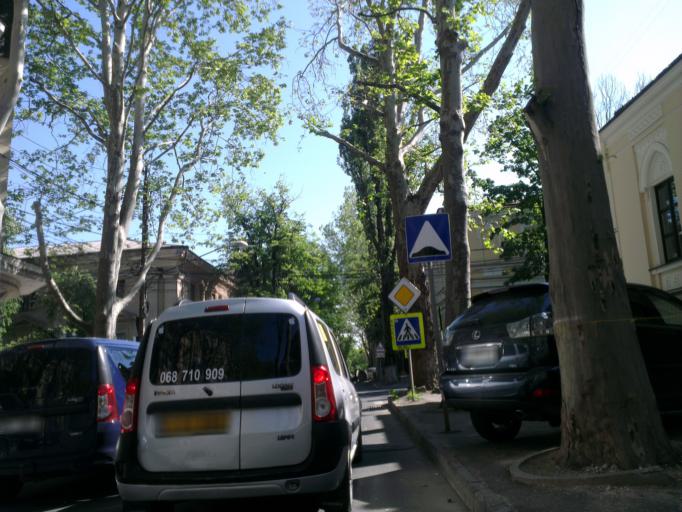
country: MD
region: Chisinau
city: Chisinau
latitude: 47.0201
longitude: 28.8344
